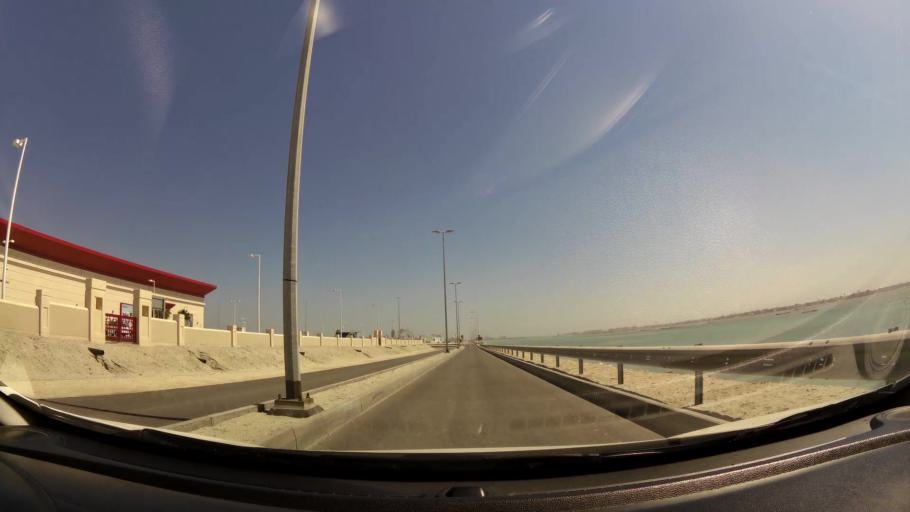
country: BH
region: Muharraq
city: Al Muharraq
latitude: 26.3044
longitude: 50.6248
